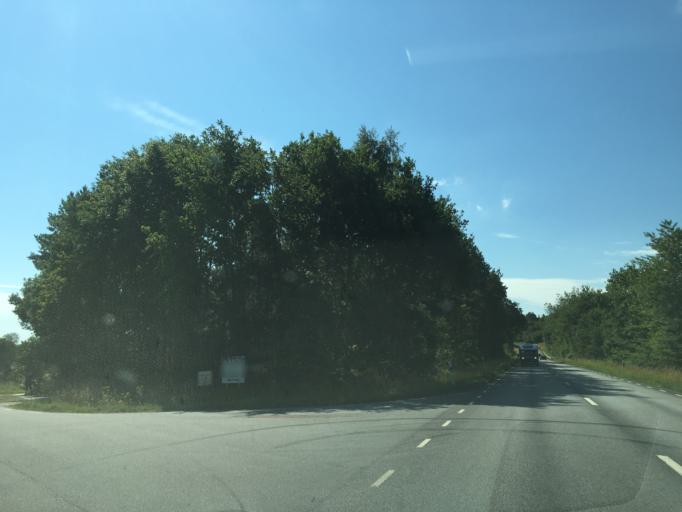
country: SE
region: Skane
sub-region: Simrishamns Kommun
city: Simrishamn
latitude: 55.6012
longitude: 14.2954
